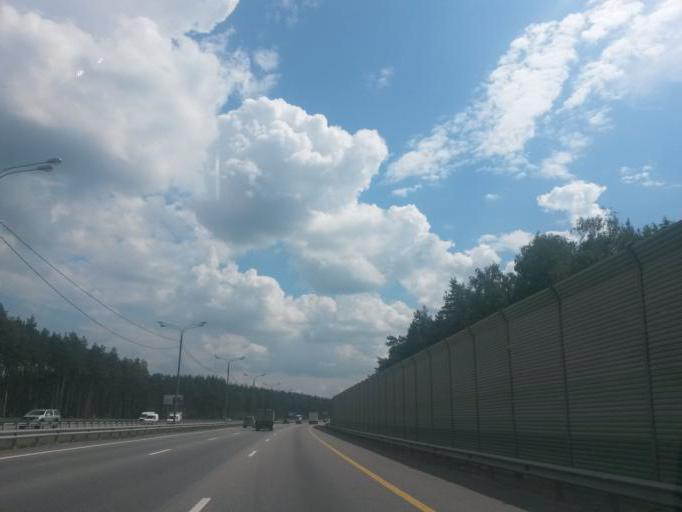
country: RU
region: Moskovskaya
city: Domodedovo
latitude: 55.4460
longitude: 37.7955
